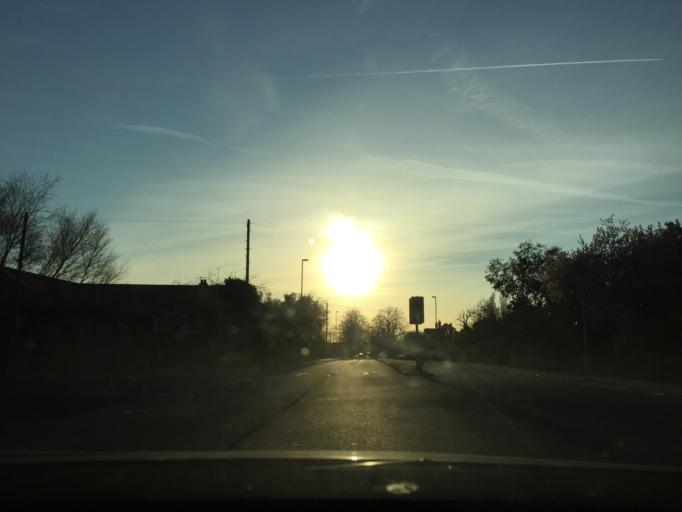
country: GB
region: England
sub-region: Portsmouth
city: Cosham
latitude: 50.8469
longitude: -1.0375
